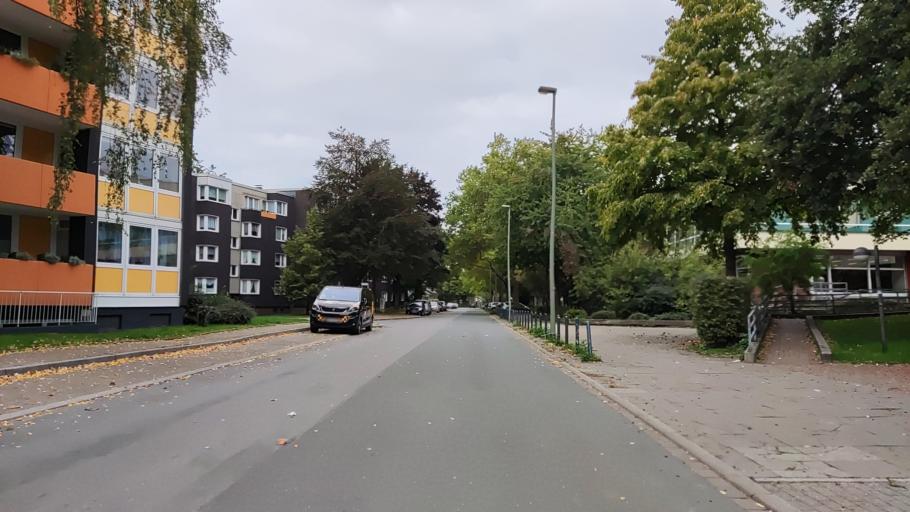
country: DE
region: North Rhine-Westphalia
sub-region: Regierungsbezirk Arnsberg
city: Herne
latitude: 51.5436
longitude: 7.2129
